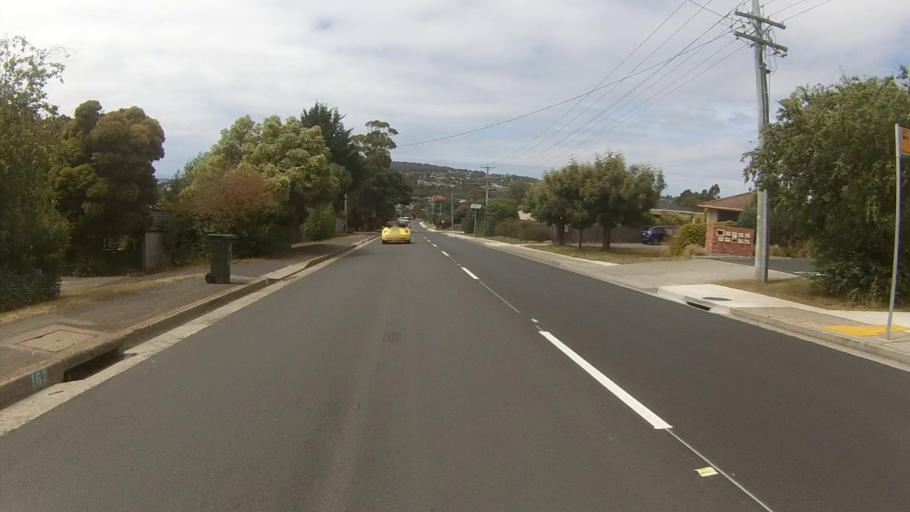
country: AU
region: Tasmania
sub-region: Kingborough
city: Kingston
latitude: -42.9695
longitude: 147.2909
